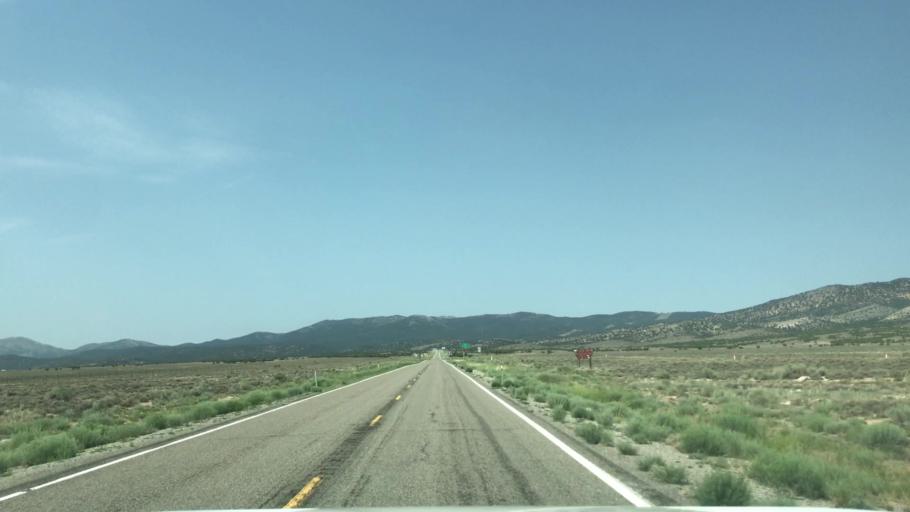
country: US
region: Nevada
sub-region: White Pine County
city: Ely
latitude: 39.0375
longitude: -114.5452
